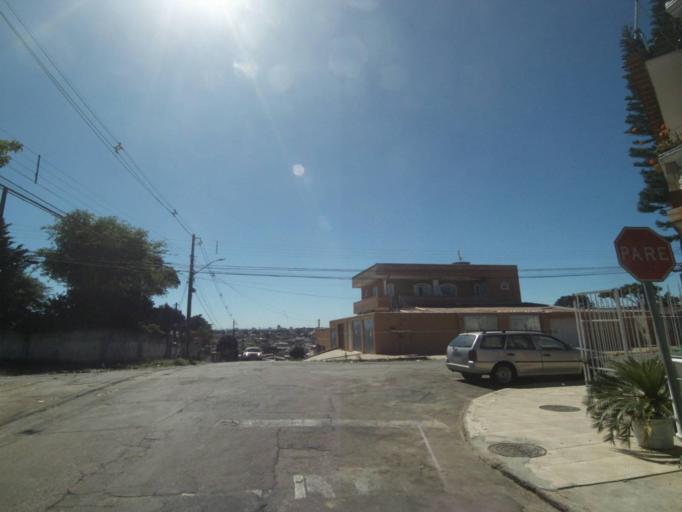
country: BR
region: Parana
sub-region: Curitiba
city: Curitiba
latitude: -25.4853
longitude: -49.3391
